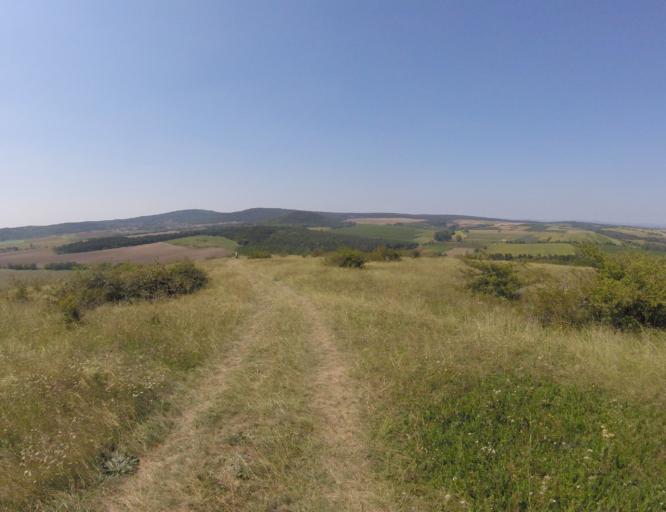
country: HU
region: Fejer
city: Pazmand
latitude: 47.2671
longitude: 18.6545
